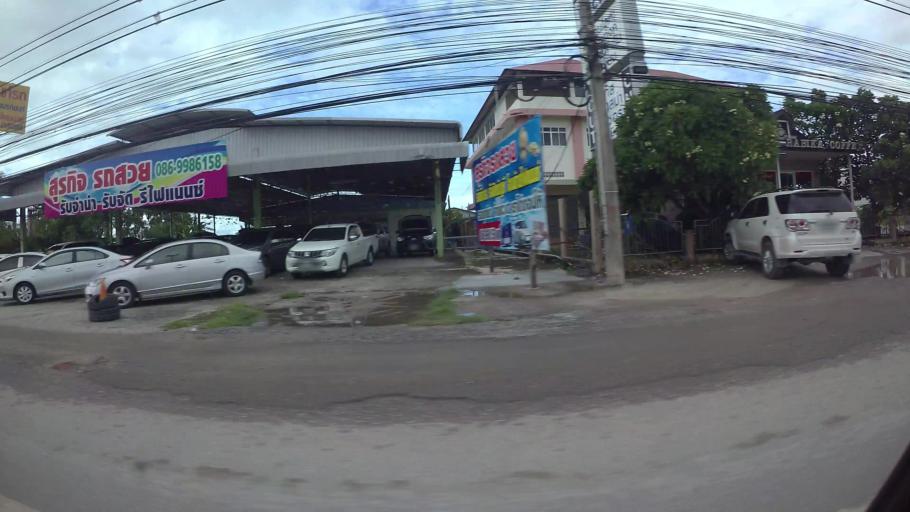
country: TH
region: Rayong
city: Rayong
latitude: 12.6985
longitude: 101.1933
